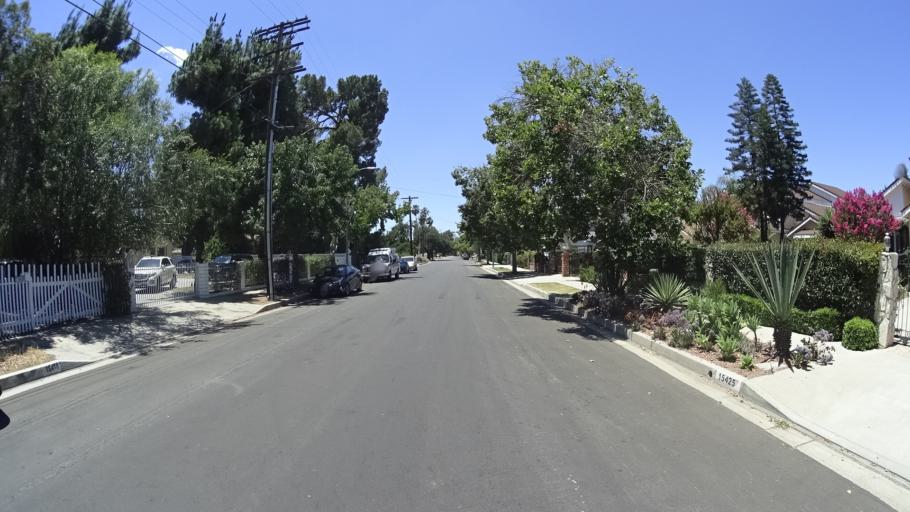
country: US
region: California
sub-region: Los Angeles County
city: Van Nuys
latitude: 34.2066
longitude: -118.4693
